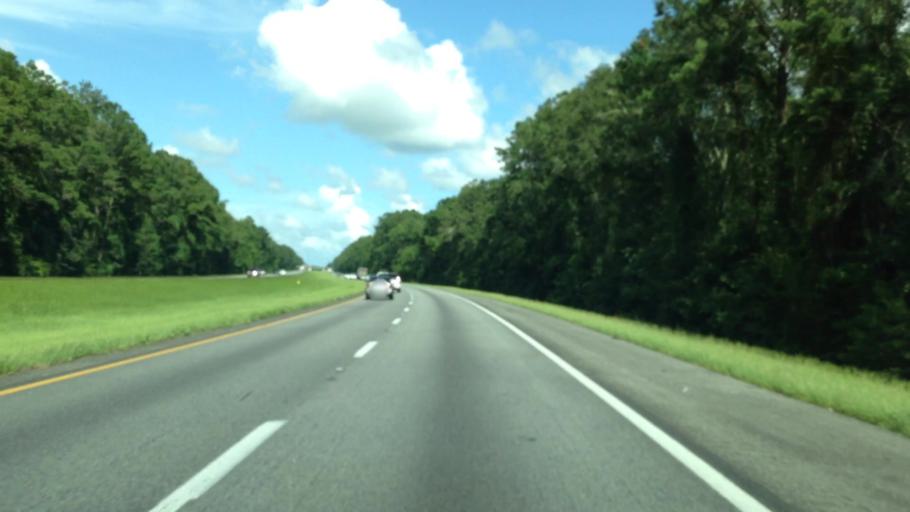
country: US
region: Florida
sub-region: Jefferson County
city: Monticello
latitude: 30.4785
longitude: -83.9382
